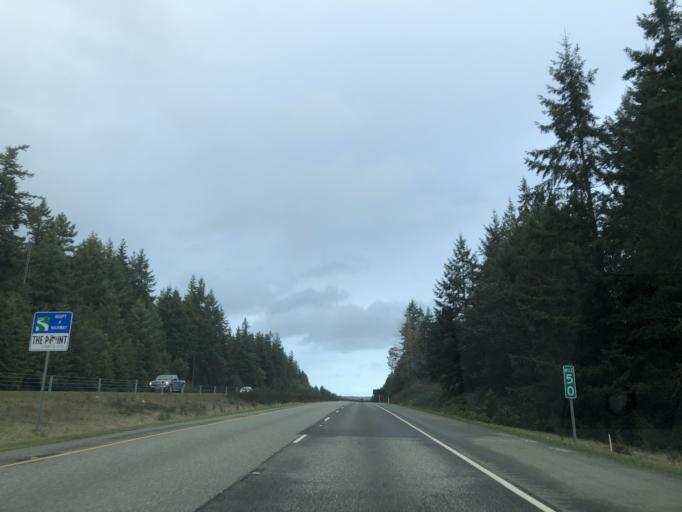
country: US
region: Washington
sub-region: Kitsap County
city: Poulsbo
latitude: 47.7225
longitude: -122.6782
